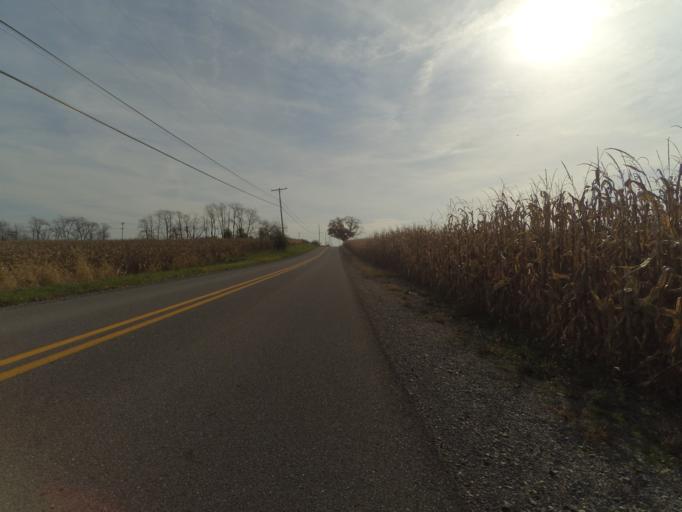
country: US
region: Pennsylvania
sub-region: Centre County
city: Houserville
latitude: 40.8520
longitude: -77.8672
